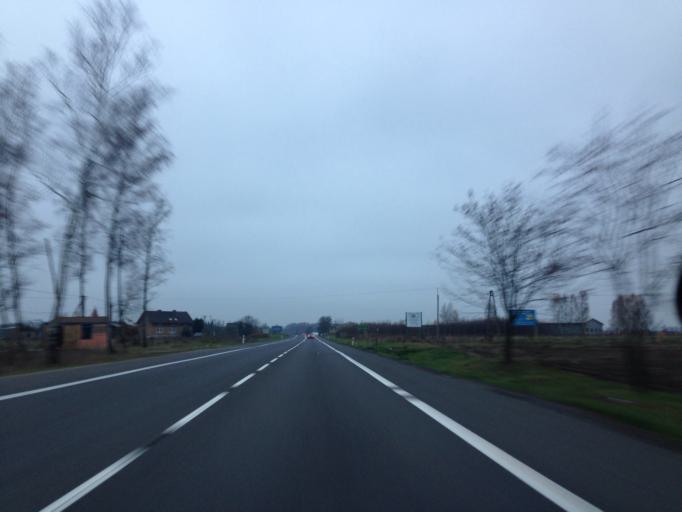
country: PL
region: Lodz Voivodeship
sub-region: Powiat zgierski
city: Strykow
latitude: 51.8782
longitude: 19.5792
